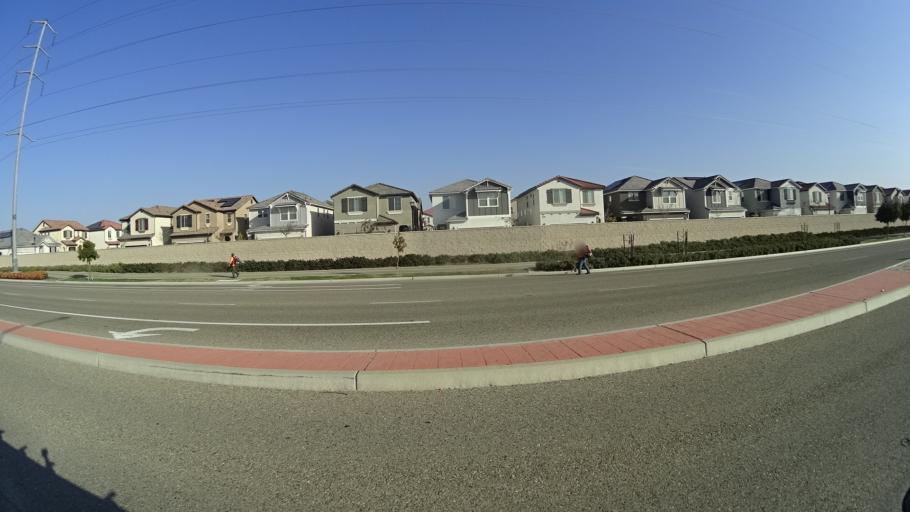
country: US
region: California
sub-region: Fresno County
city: Clovis
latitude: 36.8954
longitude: -119.7596
